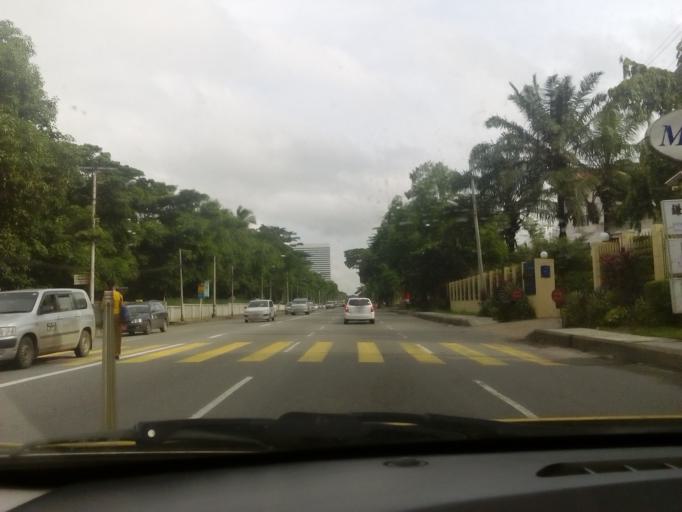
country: MM
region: Yangon
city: Yangon
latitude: 16.8376
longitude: 96.1557
